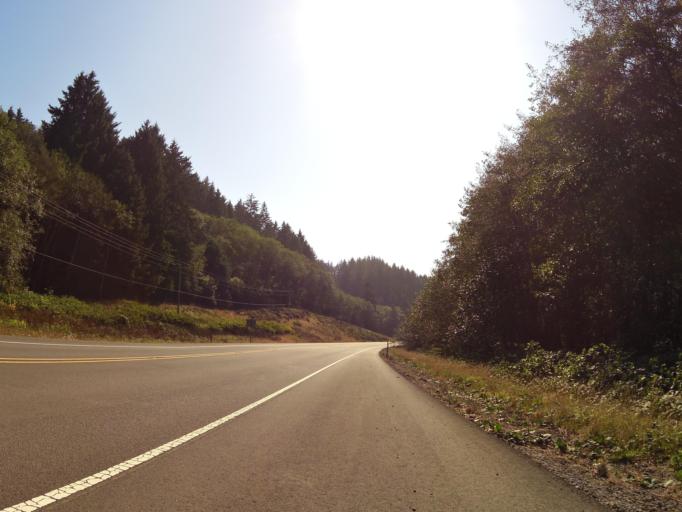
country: US
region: Oregon
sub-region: Tillamook County
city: Pacific City
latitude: 45.1516
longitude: -123.9565
